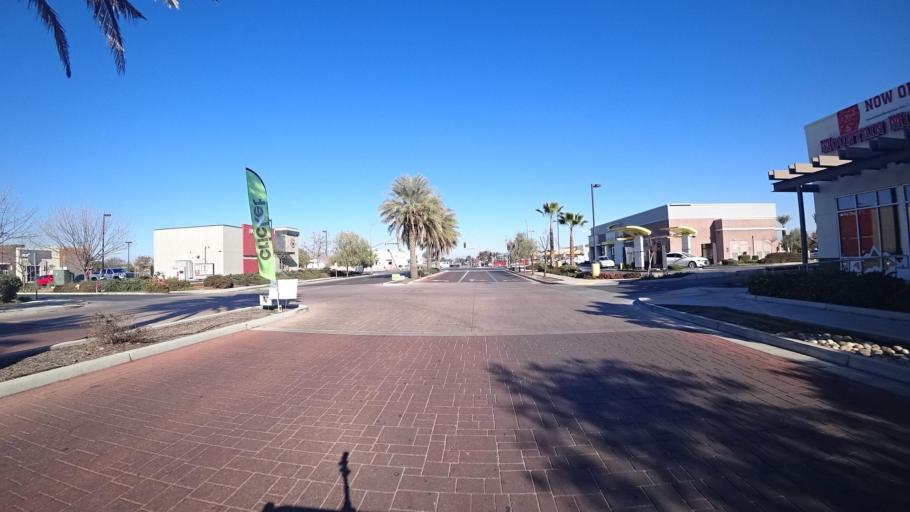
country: US
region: California
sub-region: Kern County
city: Delano
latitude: 35.7460
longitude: -119.2472
